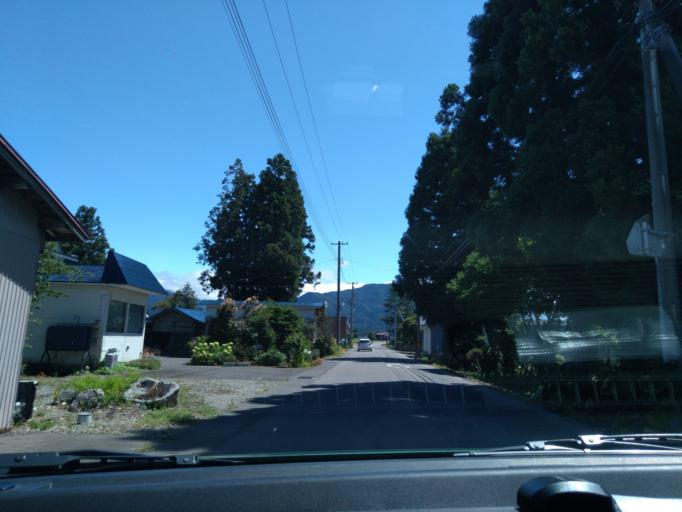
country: JP
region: Akita
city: Kakunodatemachi
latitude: 39.5280
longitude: 140.6098
